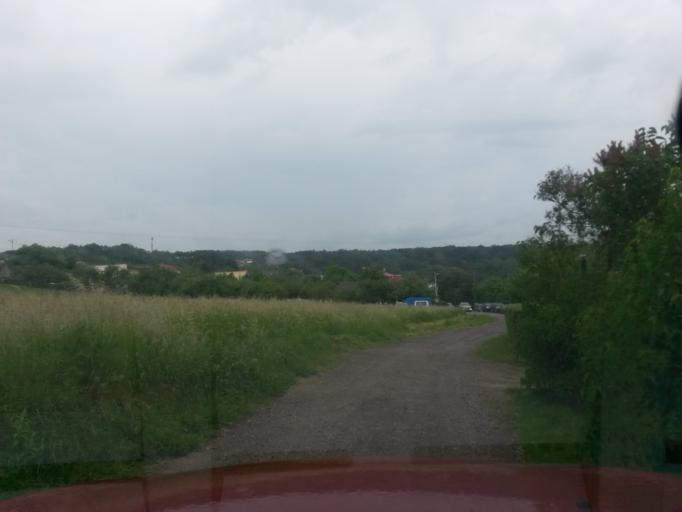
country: SK
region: Kosicky
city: Kosice
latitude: 48.7024
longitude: 21.1804
